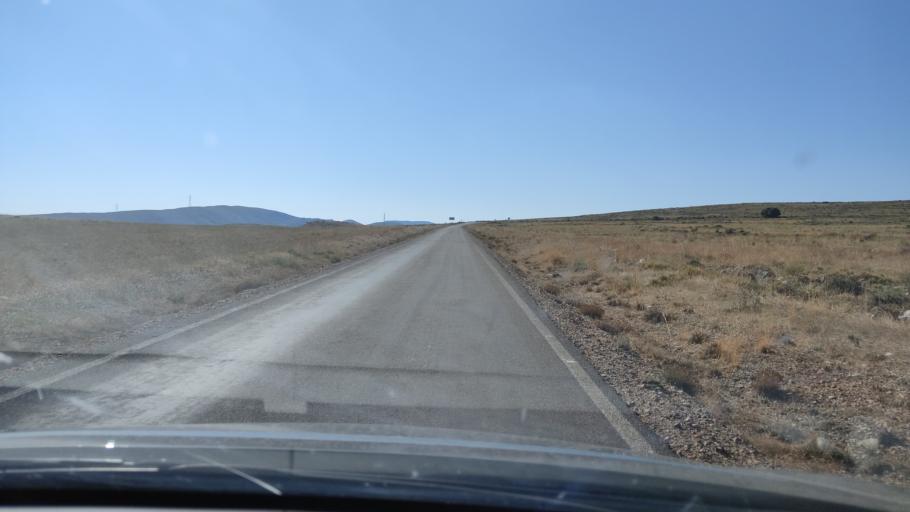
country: ES
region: Aragon
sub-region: Provincia de Teruel
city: Anadon
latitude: 41.0223
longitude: -0.9629
